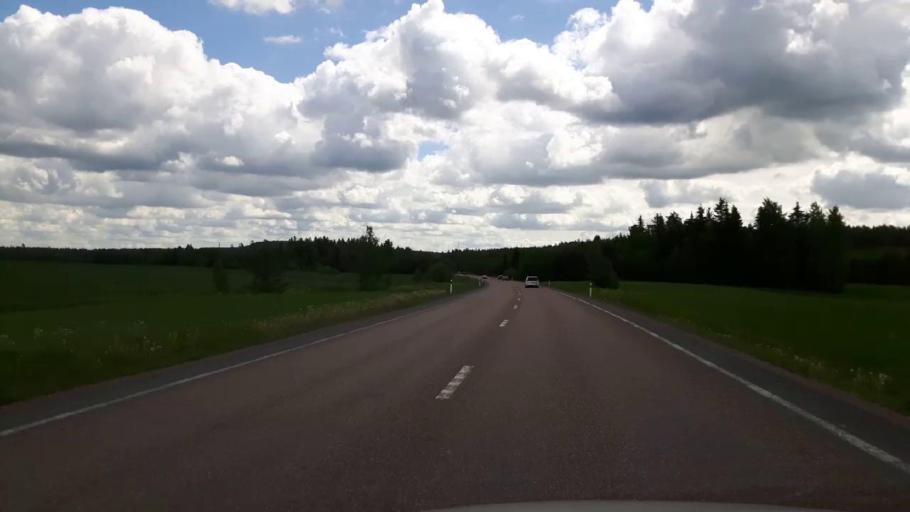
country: SE
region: Dalarna
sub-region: Saters Kommun
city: Saeter
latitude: 60.5015
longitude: 15.7448
